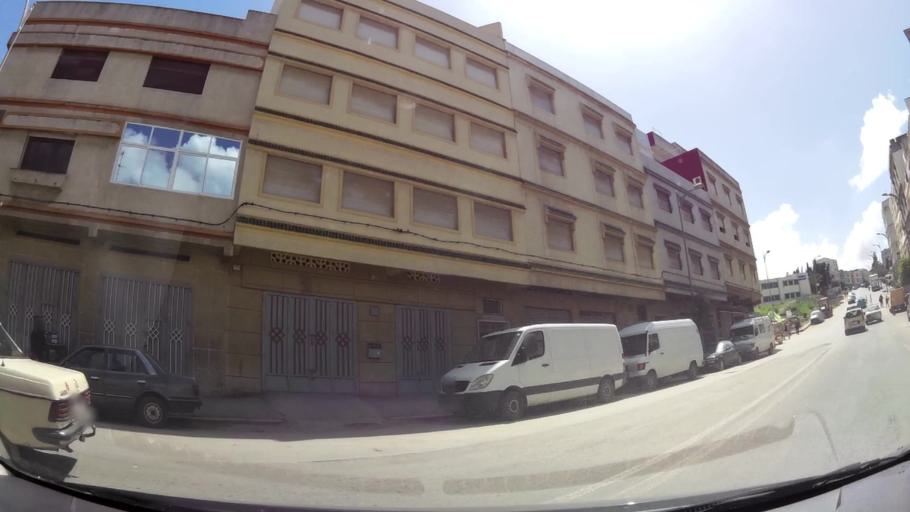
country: MA
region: Tanger-Tetouan
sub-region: Tanger-Assilah
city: Tangier
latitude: 35.7578
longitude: -5.8236
